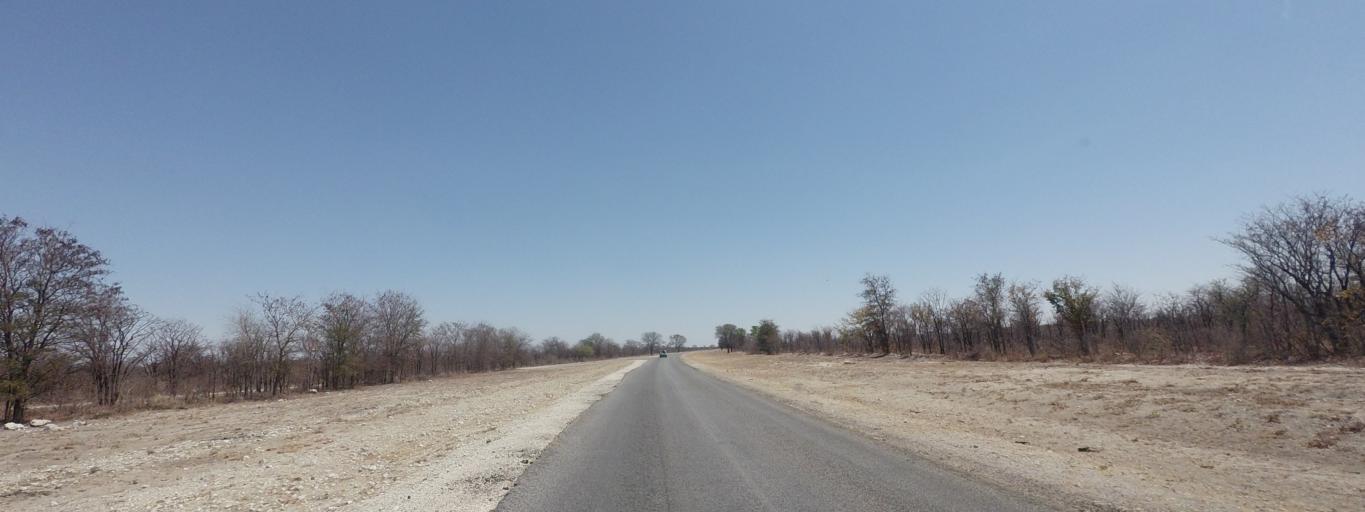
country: BW
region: Central
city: Nata
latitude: -20.3723
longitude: 26.3221
